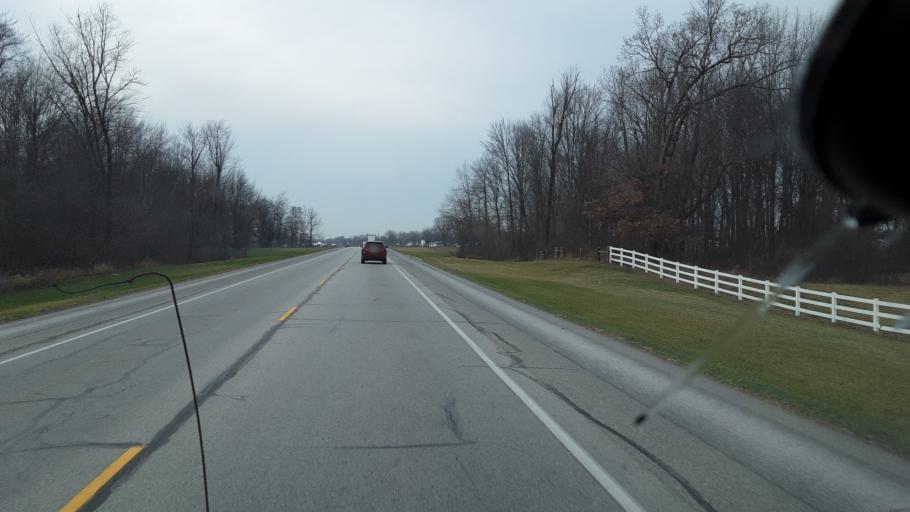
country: US
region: Indiana
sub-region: LaGrange County
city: Topeka
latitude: 41.6504
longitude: -85.5667
